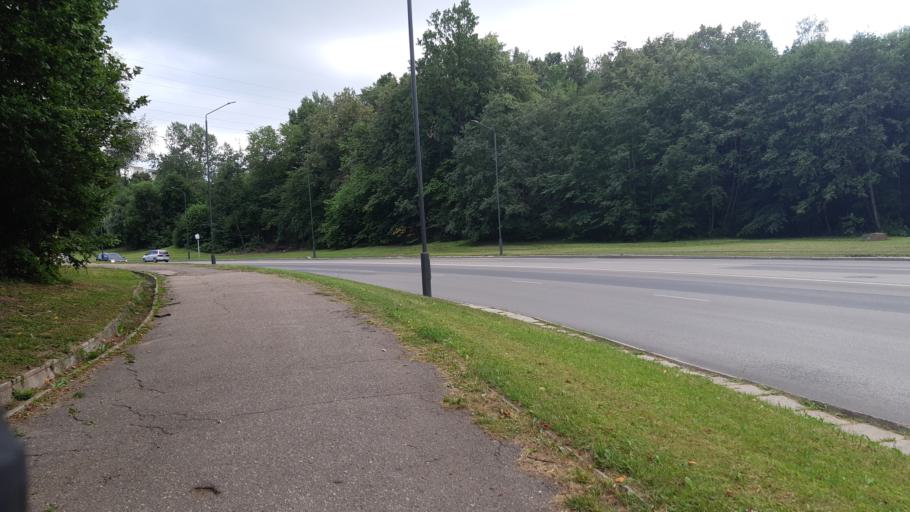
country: LT
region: Kauno apskritis
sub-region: Kaunas
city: Eiguliai
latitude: 54.9282
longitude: 23.9203
